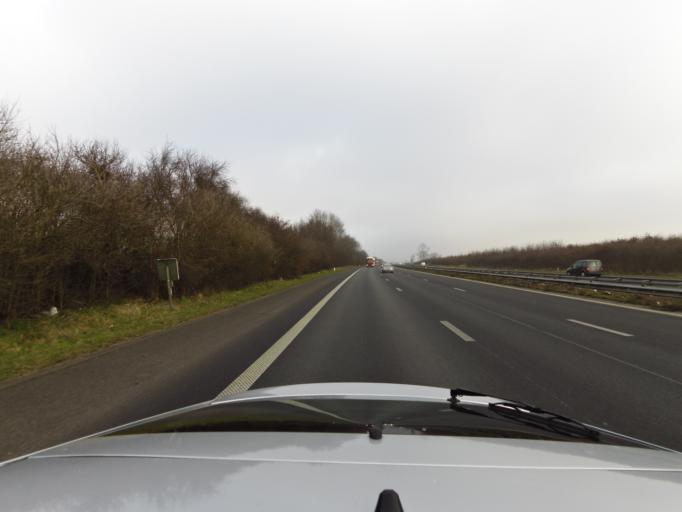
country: BE
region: Flanders
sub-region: Provincie West-Vlaanderen
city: Ledegem
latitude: 50.8603
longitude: 3.1711
